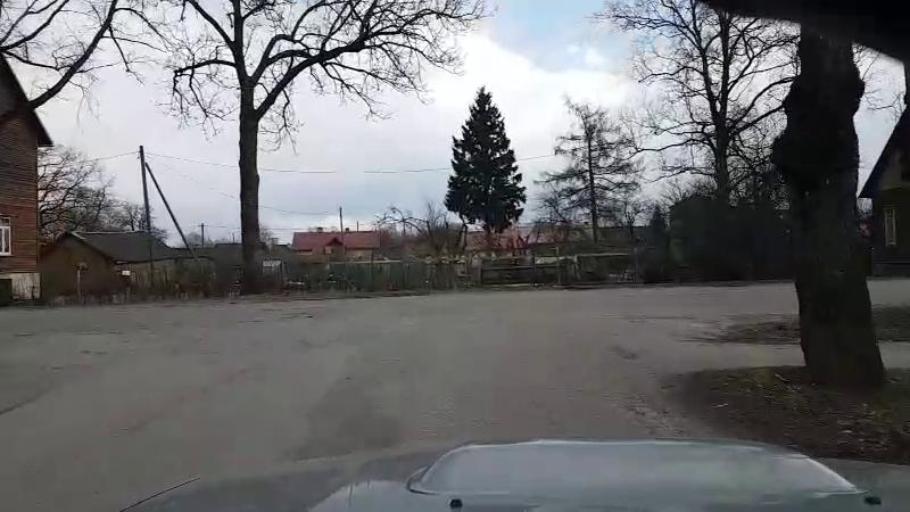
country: EE
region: Jaervamaa
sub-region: Paide linn
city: Paide
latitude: 58.8855
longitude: 25.5514
